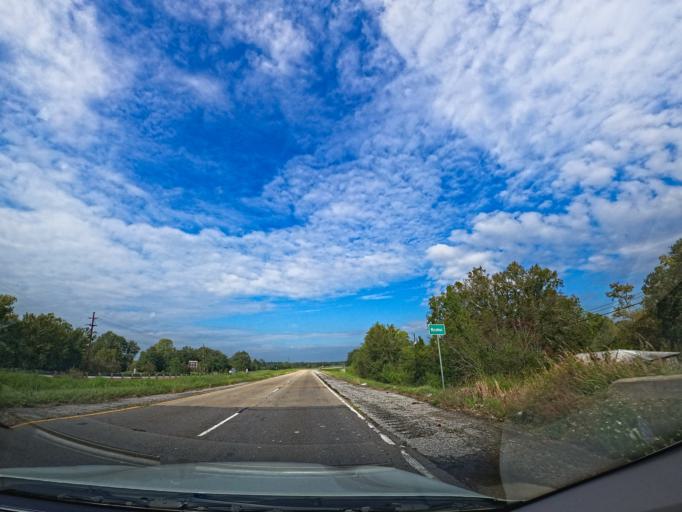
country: US
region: Louisiana
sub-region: Saint Mary Parish
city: Patterson
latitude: 29.6996
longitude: -91.3754
